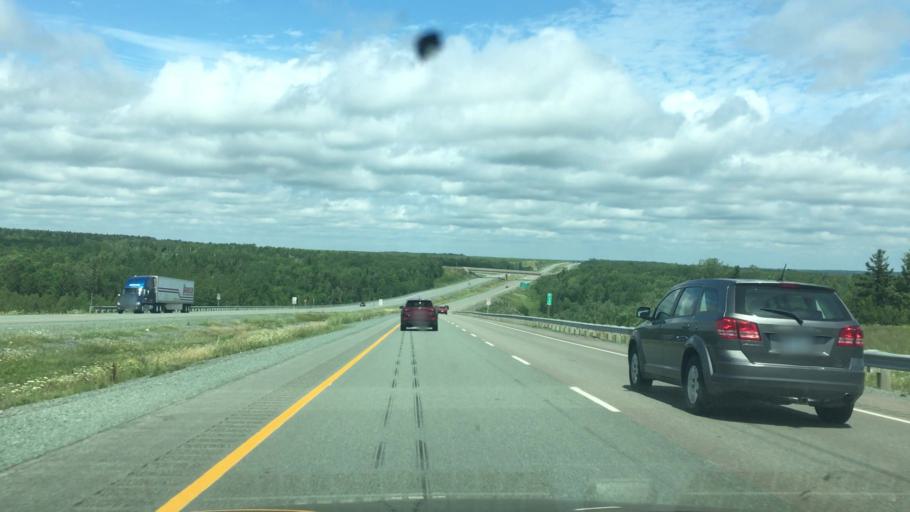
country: CA
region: Nova Scotia
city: Oxford
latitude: 45.6004
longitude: -63.7314
